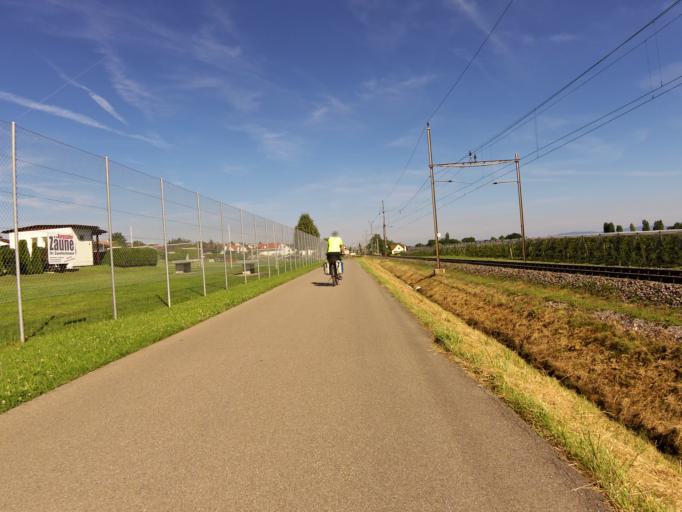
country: CH
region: Thurgau
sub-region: Kreuzlingen District
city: Altnau
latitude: 47.6189
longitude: 9.2715
